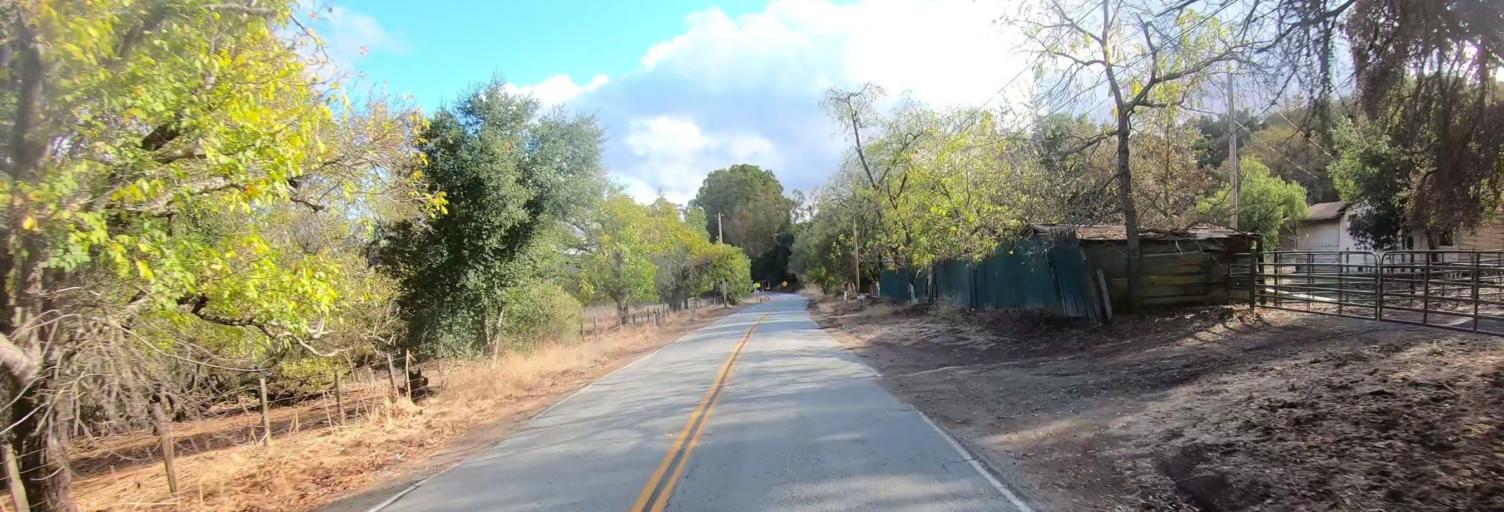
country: US
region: California
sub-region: Santa Clara County
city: East Foothills
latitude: 37.3447
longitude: -121.7247
